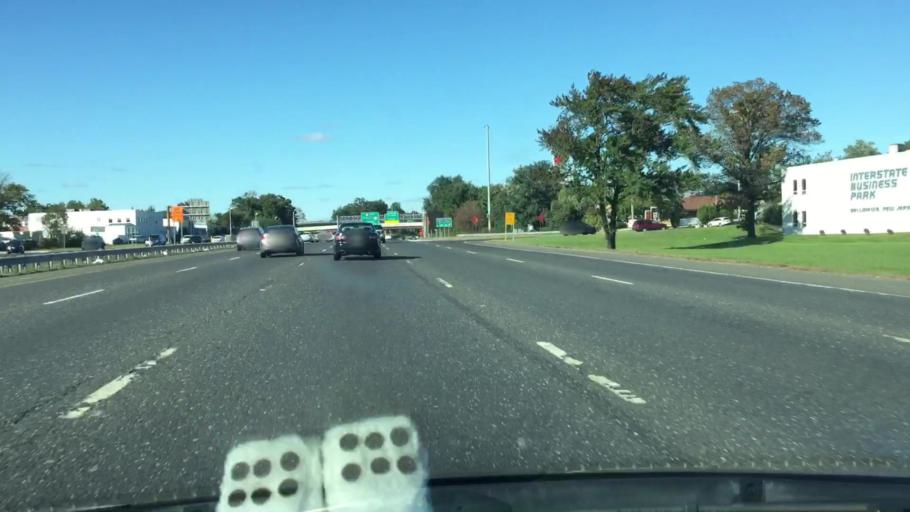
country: US
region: New Jersey
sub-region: Camden County
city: Bellmawr
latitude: 39.8619
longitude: -75.1001
